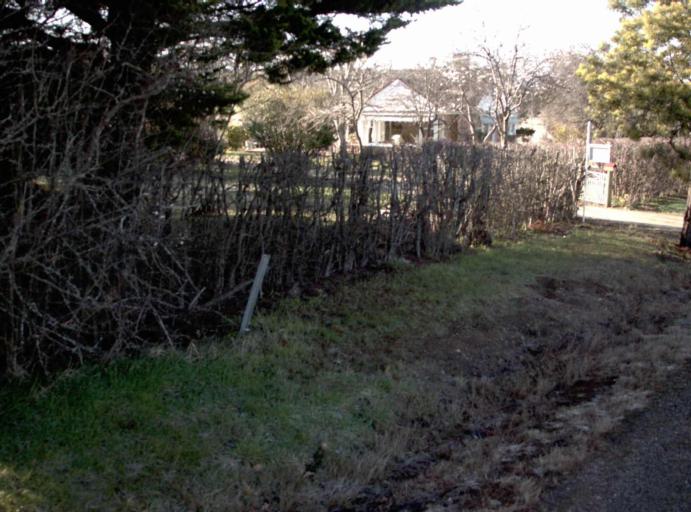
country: AU
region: Tasmania
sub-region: Launceston
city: Newstead
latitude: -41.4687
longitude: 147.2095
